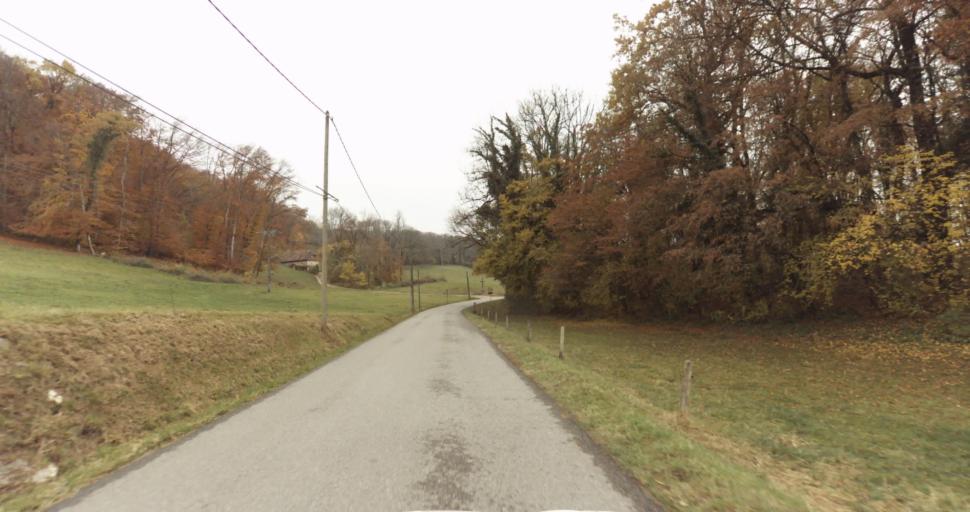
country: FR
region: Rhone-Alpes
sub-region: Departement de la Haute-Savoie
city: Cusy
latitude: 45.7546
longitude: 6.0174
